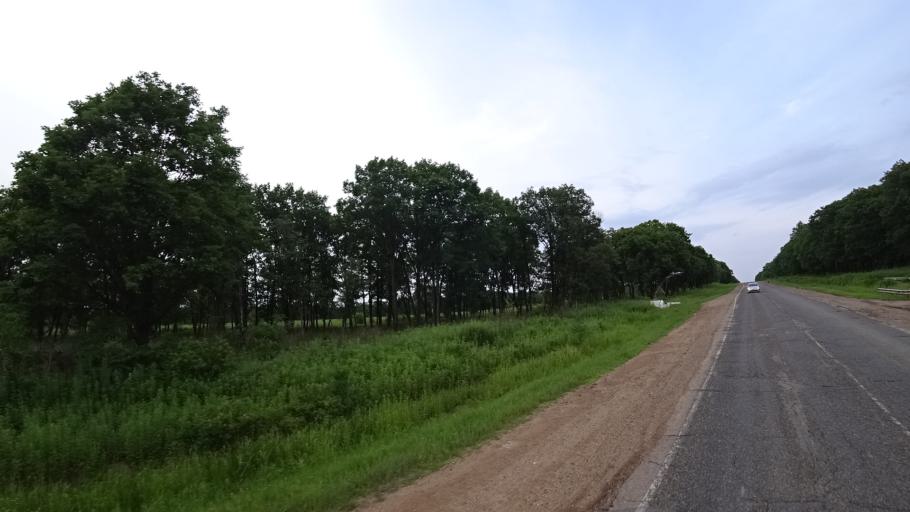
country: RU
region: Primorskiy
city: Novosysoyevka
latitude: 44.2353
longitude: 133.3850
